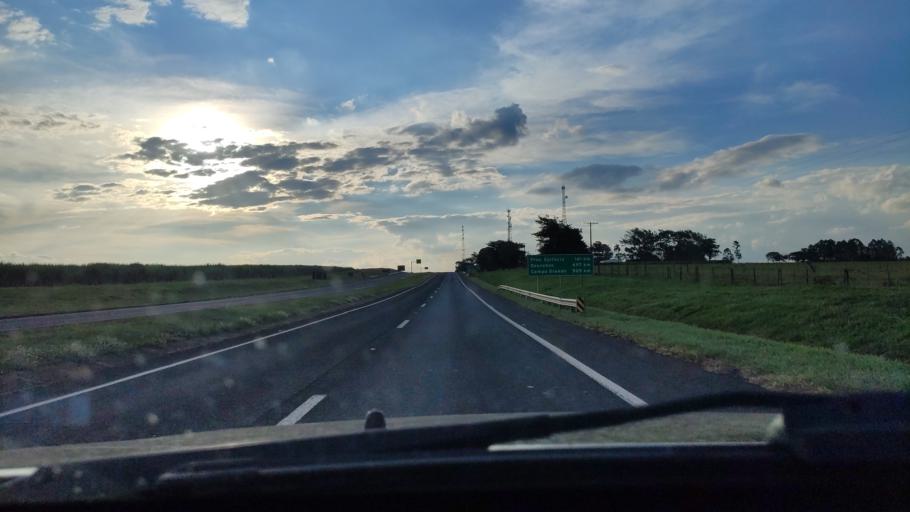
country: BR
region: Sao Paulo
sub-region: Rancharia
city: Rancharia
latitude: -22.4321
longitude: -51.0133
